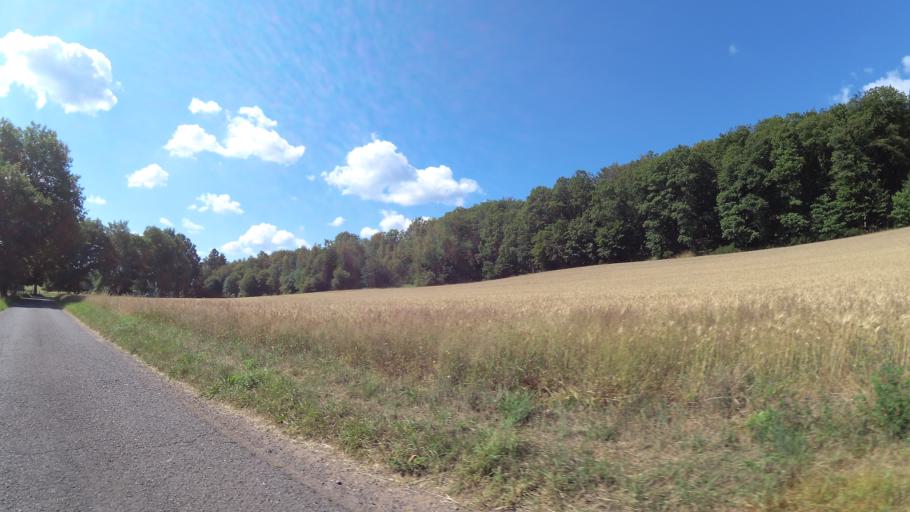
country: DE
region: Saarland
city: Weiskirchen
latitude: 49.5131
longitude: 6.8221
